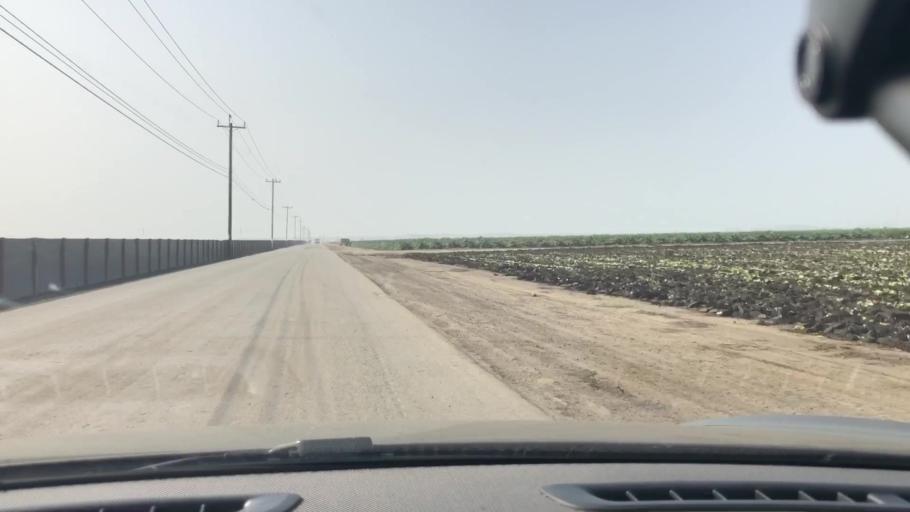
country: US
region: California
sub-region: Monterey County
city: Castroville
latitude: 36.7499
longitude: -121.7758
